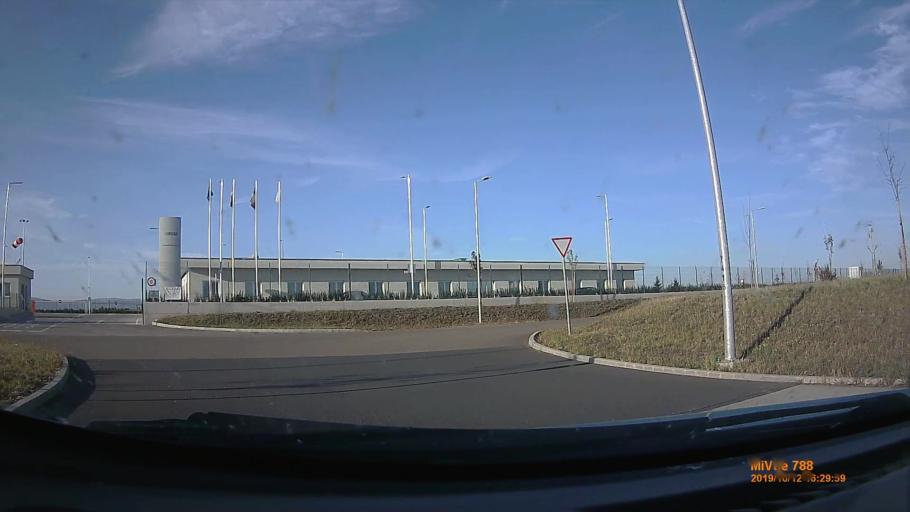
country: HU
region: Heves
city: Adacs
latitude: 47.7243
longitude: 19.9619
